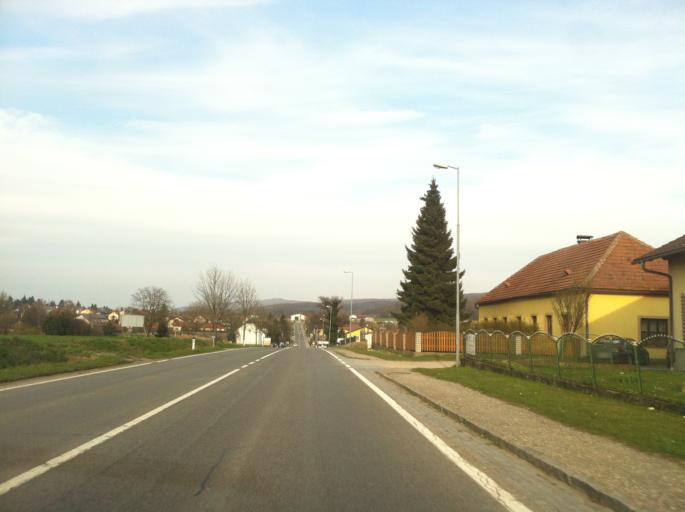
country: AT
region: Lower Austria
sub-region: Politischer Bezirk Tulln
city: Sieghartskirchen
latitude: 48.2554
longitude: 16.0636
